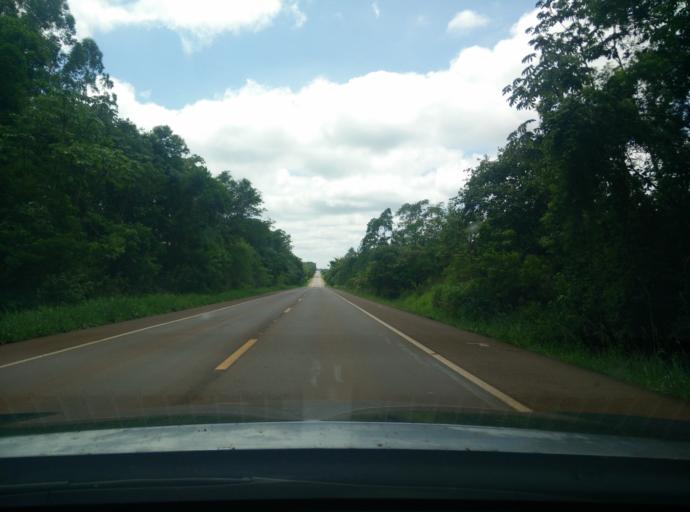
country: BR
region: Parana
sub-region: Campo Mourao
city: Campo Mourao
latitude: -23.9803
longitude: -52.5368
